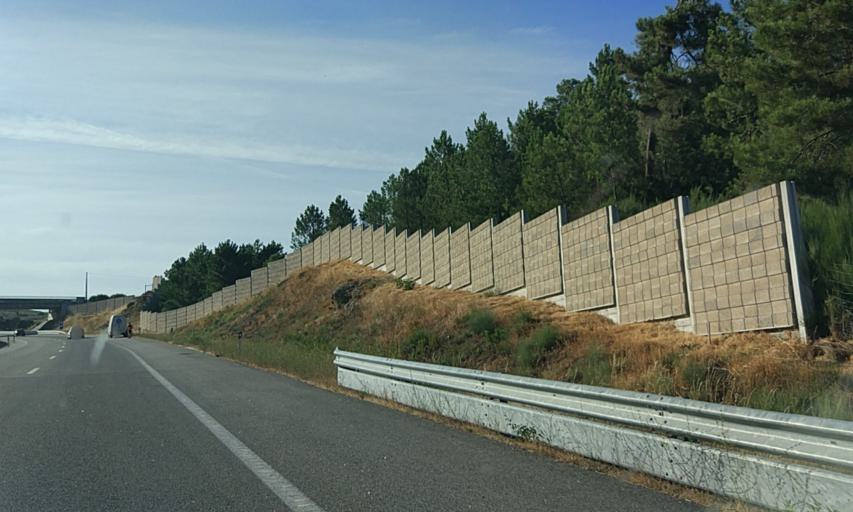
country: PT
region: Vila Real
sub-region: Murca
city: Murca
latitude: 41.3855
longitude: -7.5044
